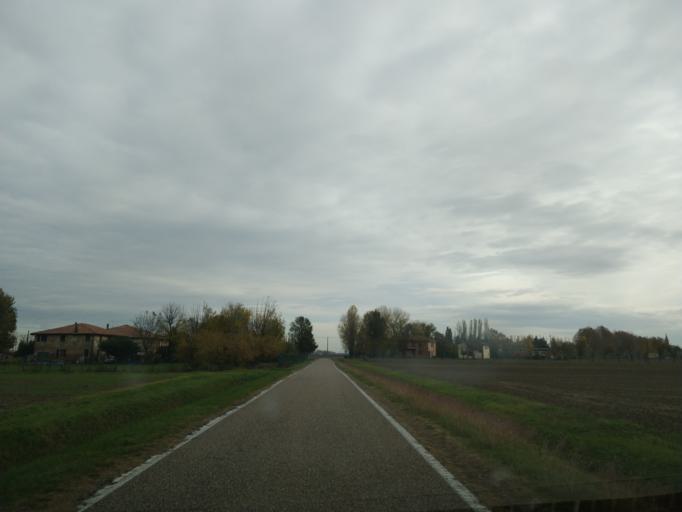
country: IT
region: Emilia-Romagna
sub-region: Provincia di Bologna
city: Argelato
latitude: 44.6192
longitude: 11.3210
